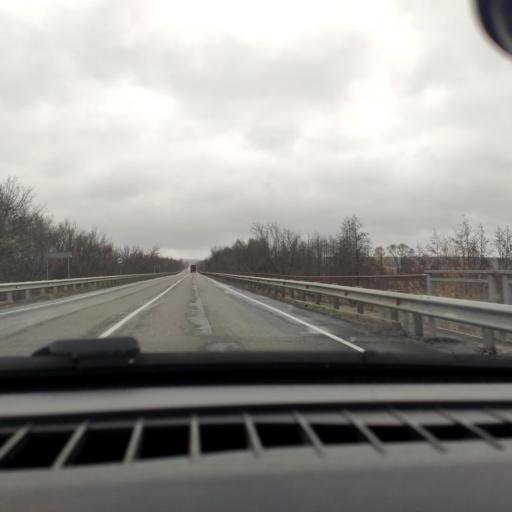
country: RU
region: Voronezj
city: Ostrogozhsk
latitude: 51.0392
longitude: 38.9818
